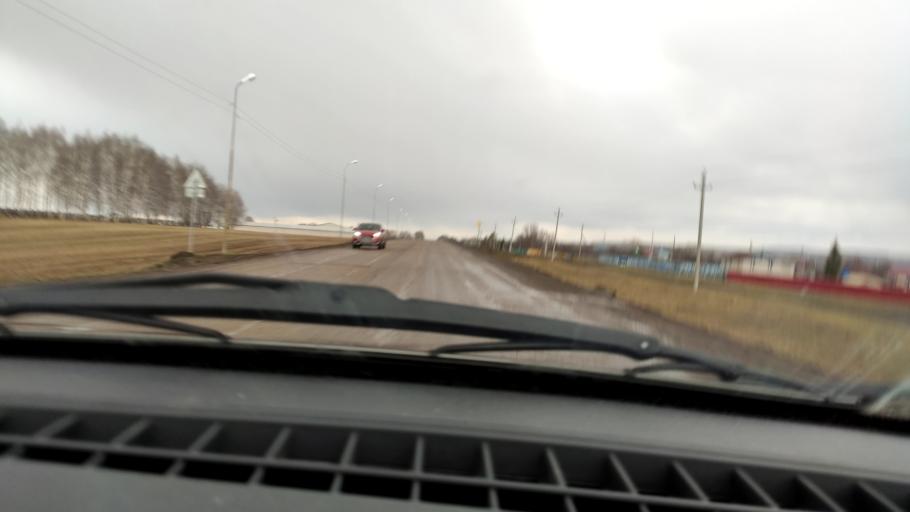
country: RU
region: Bashkortostan
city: Chekmagush
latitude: 55.1166
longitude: 54.8324
